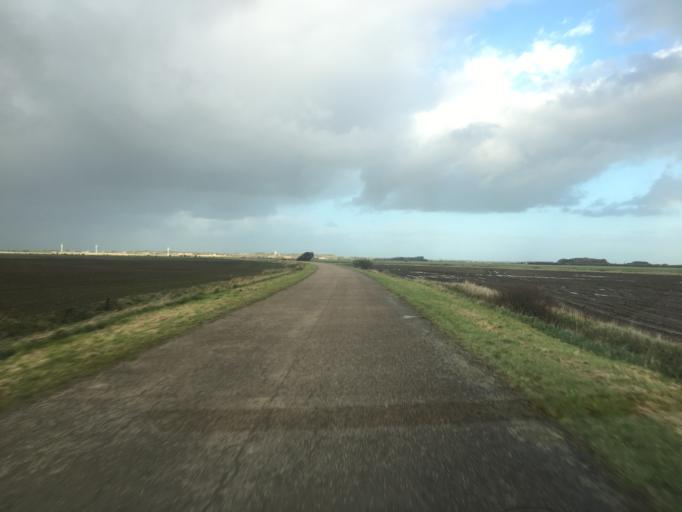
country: DE
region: Schleswig-Holstein
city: Aventoft
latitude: 54.9197
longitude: 8.7631
